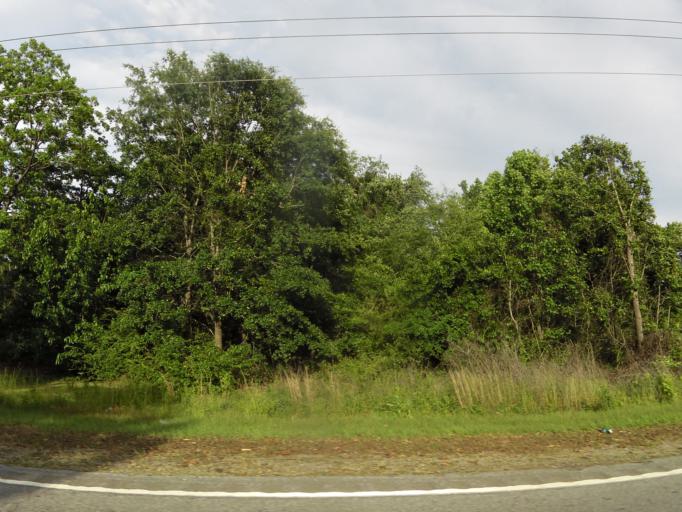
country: US
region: South Carolina
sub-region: Hampton County
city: Estill
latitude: 32.7295
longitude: -81.2419
